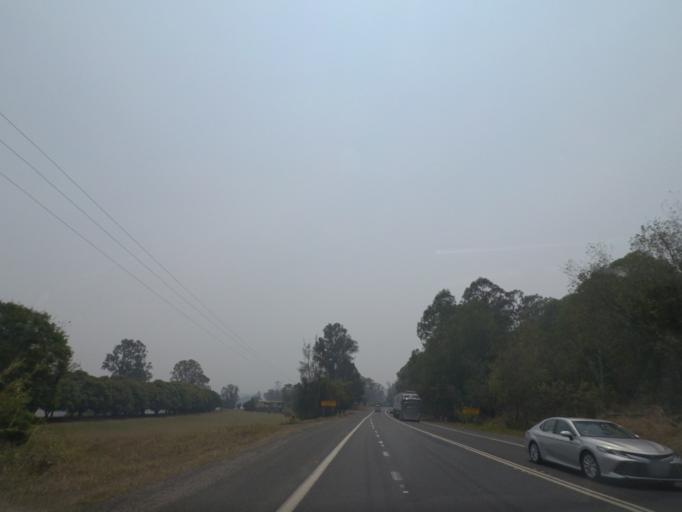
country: AU
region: New South Wales
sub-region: Clarence Valley
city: Maclean
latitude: -29.5551
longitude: 153.1521
